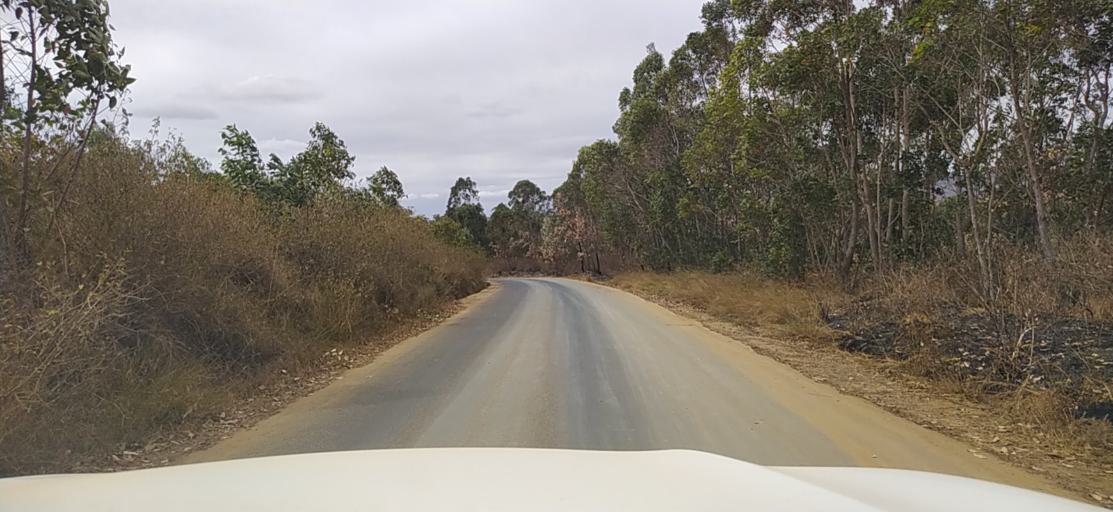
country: MG
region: Alaotra Mangoro
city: Ambatondrazaka
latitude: -17.9349
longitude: 48.2508
